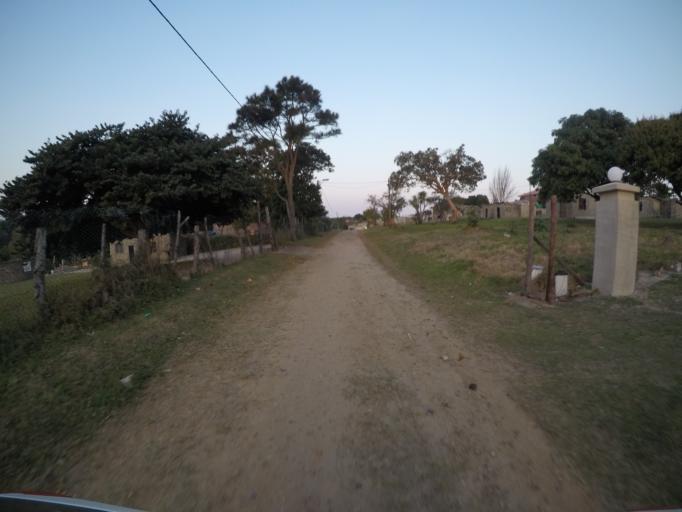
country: ZA
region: KwaZulu-Natal
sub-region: uThungulu District Municipality
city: Richards Bay
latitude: -28.7581
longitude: 32.1254
